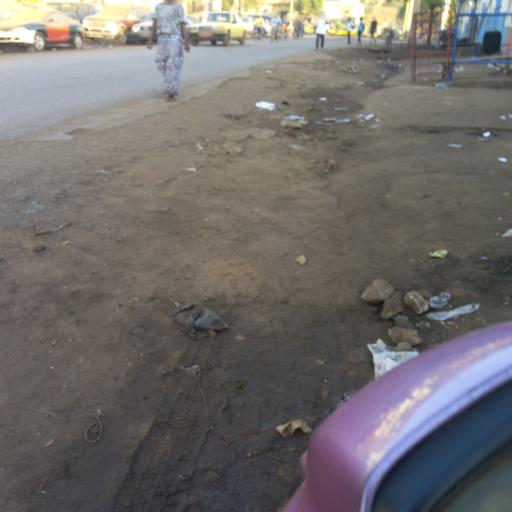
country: ML
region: Bamako
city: Bamako
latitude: 12.6620
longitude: -7.9818
